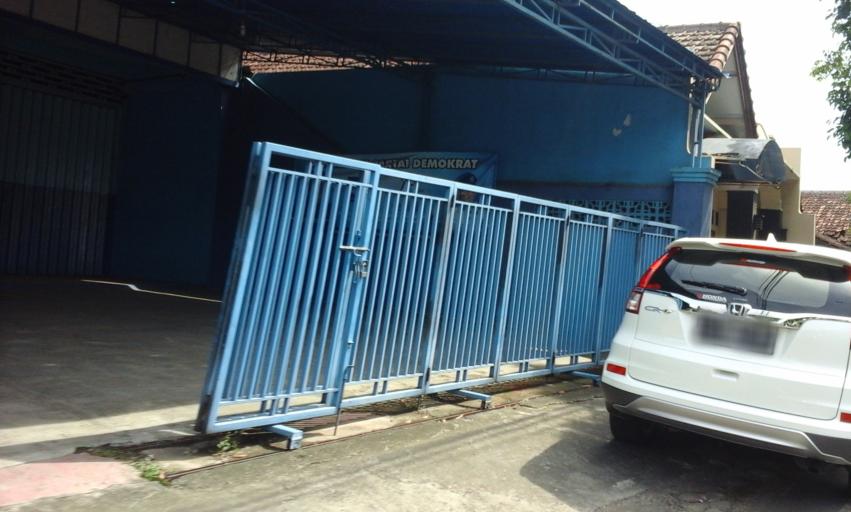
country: ID
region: East Java
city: Krajan
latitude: -8.2402
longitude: 114.3553
